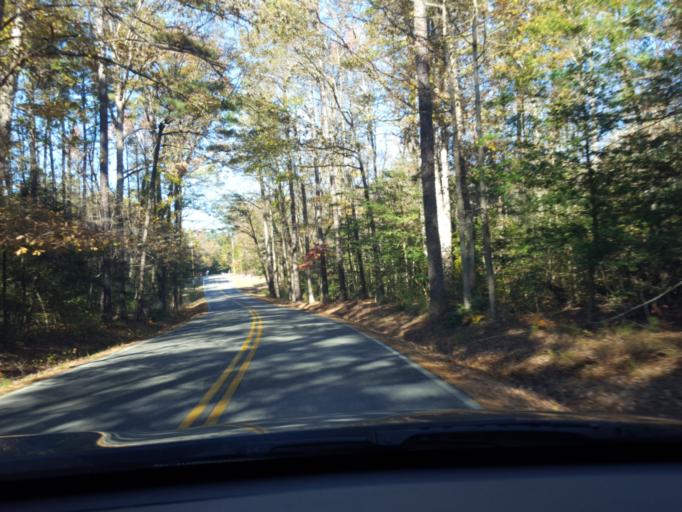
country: US
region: Maryland
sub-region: Saint Mary's County
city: California
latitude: 38.2385
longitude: -76.5432
